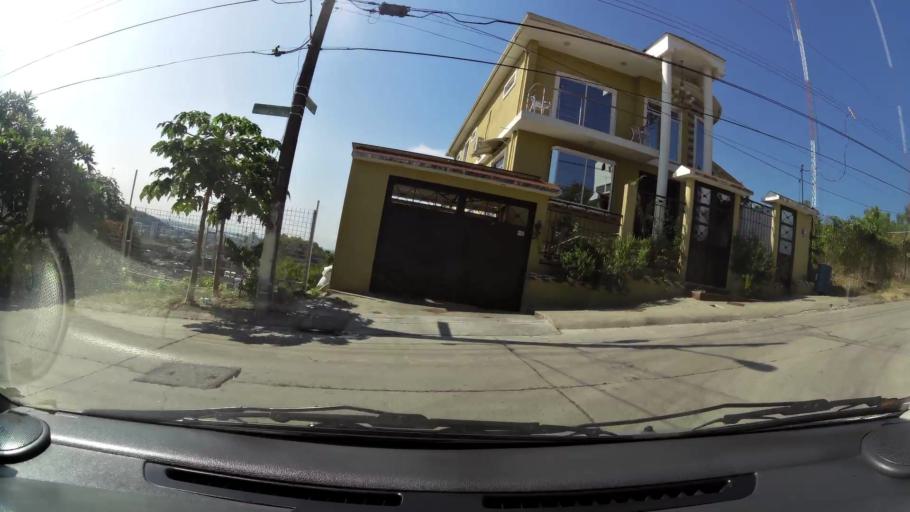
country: EC
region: Guayas
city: Guayaquil
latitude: -2.1825
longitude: -79.9138
